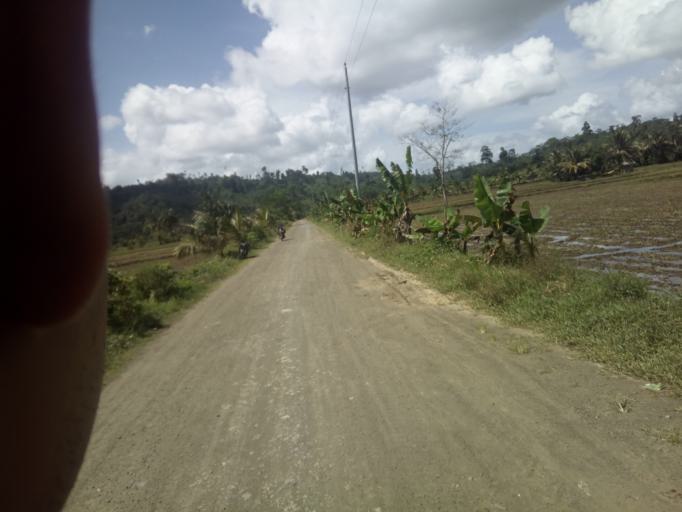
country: PH
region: Caraga
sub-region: Province of Agusan del Sur
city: Santa Josefa
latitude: 7.9804
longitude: 125.9820
